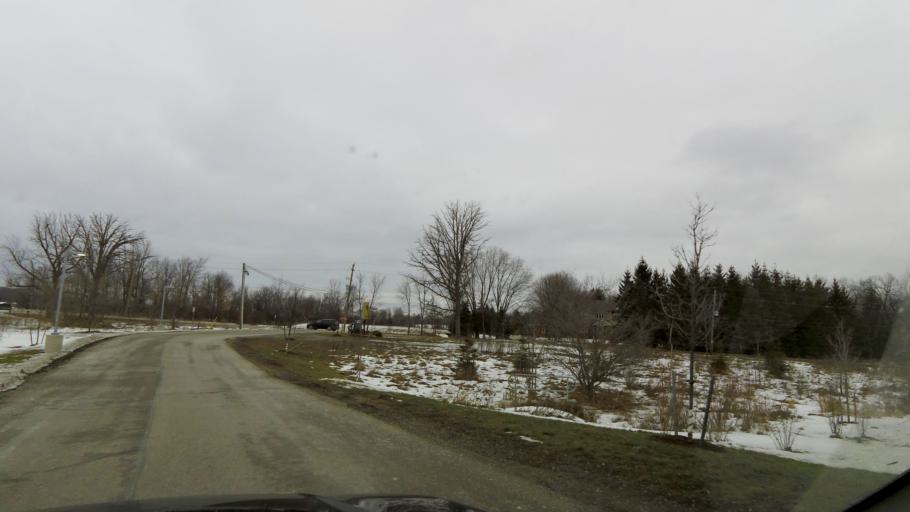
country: CA
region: Ontario
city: Brampton
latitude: 43.8766
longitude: -79.8535
